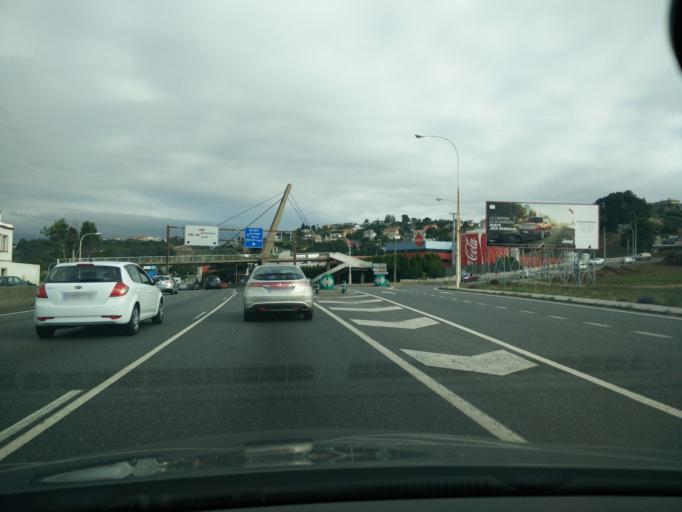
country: ES
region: Galicia
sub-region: Provincia da Coruna
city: A Coruna
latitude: 43.3324
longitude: -8.4012
